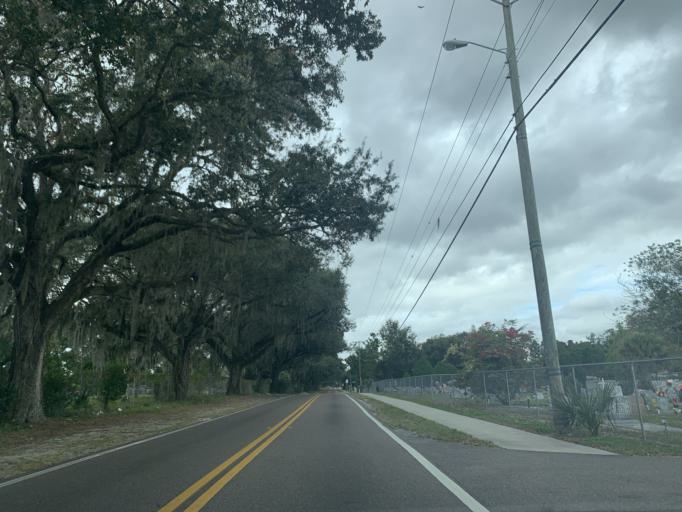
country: US
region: Florida
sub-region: Hillsborough County
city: East Lake-Orient Park
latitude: 27.9852
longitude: -82.4005
